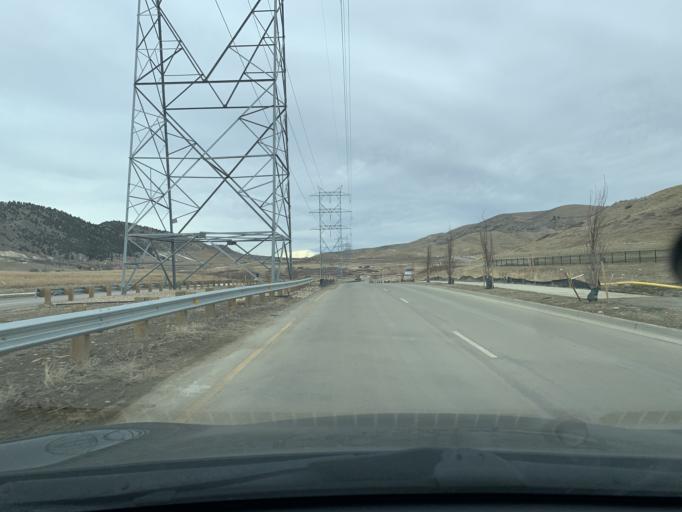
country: US
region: Colorado
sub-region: Jefferson County
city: West Pleasant View
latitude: 39.6762
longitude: -105.1831
